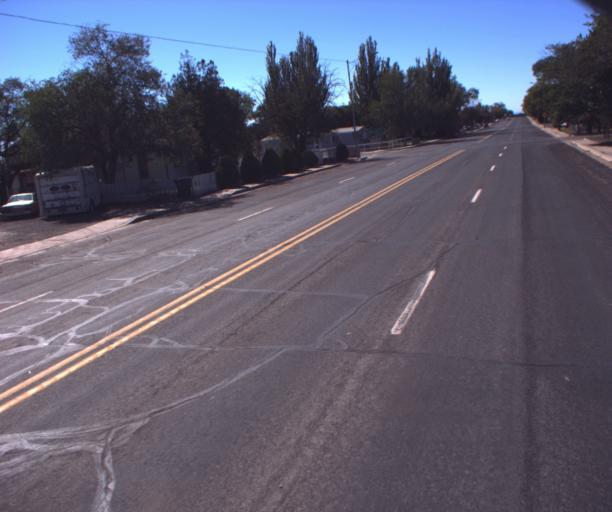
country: US
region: Arizona
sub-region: Navajo County
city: Joseph City
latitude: 34.9560
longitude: -110.3306
